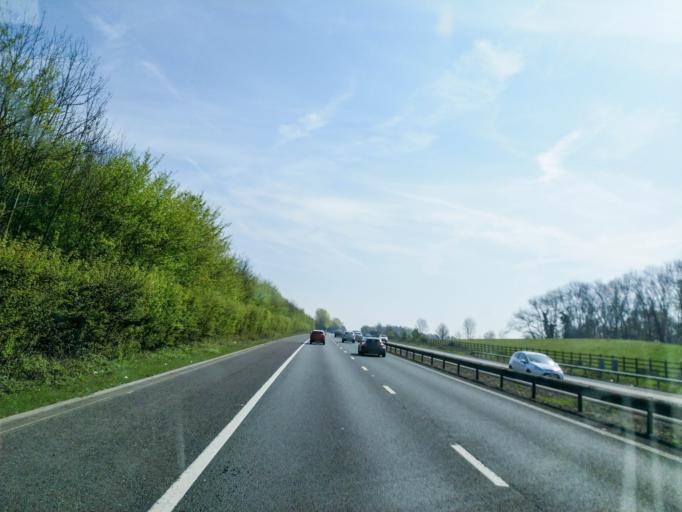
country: GB
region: England
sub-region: Kent
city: Kemsing
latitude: 51.3014
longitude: 0.2452
